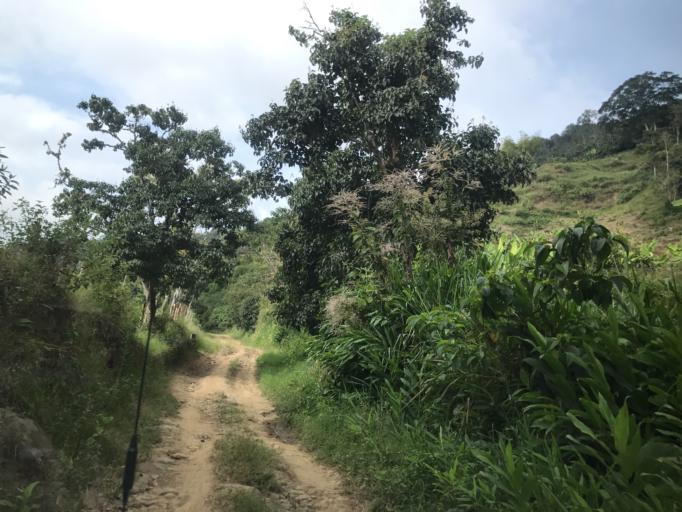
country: CO
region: Valle del Cauca
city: Obando
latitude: 4.5715
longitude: -75.8899
